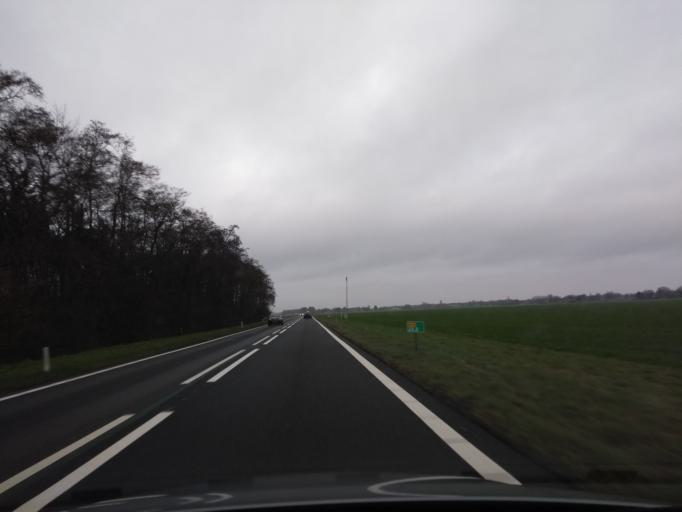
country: NL
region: Overijssel
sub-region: Gemeente Twenterand
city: Westerhaar-Vriezenveensewijk
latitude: 52.4879
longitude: 6.6010
